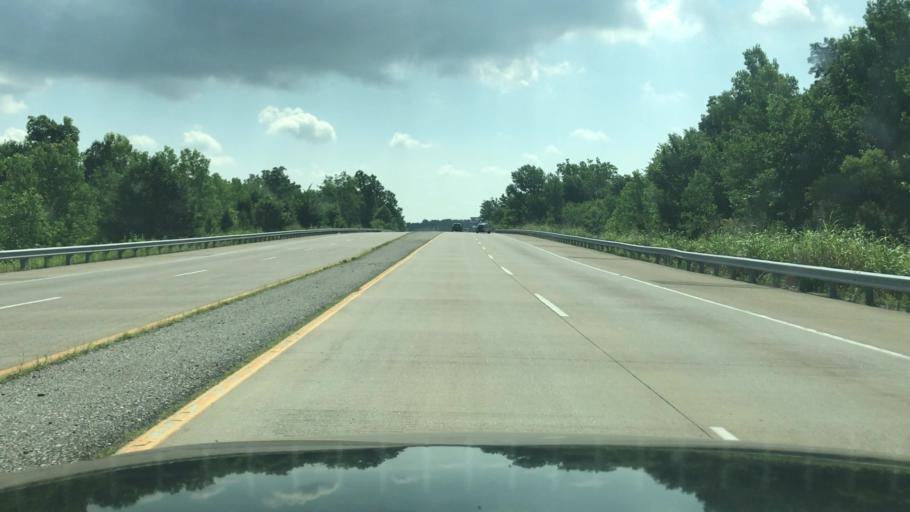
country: US
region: Indiana
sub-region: Vanderburgh County
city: Melody Hill
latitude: 38.0129
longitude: -87.4981
